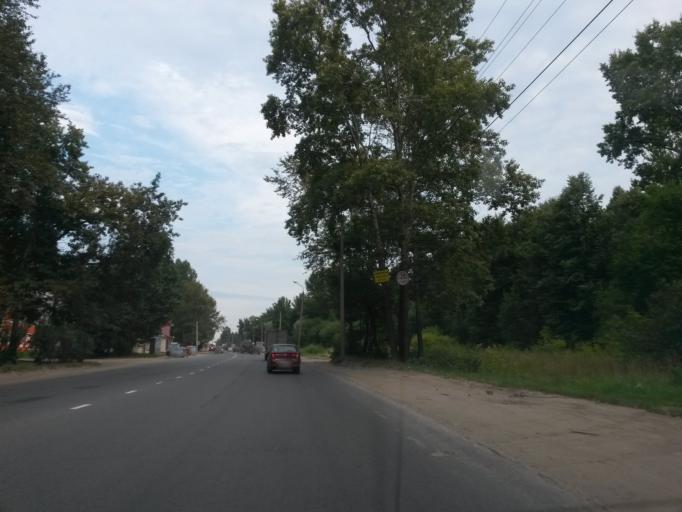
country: RU
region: Jaroslavl
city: Yaroslavl
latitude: 57.5838
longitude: 39.8241
